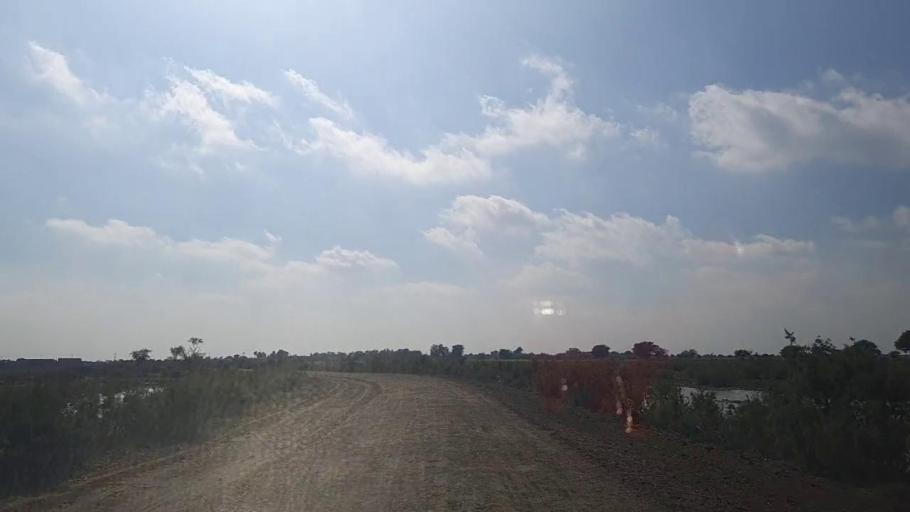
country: PK
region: Sindh
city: Sanghar
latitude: 26.0526
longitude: 69.0048
